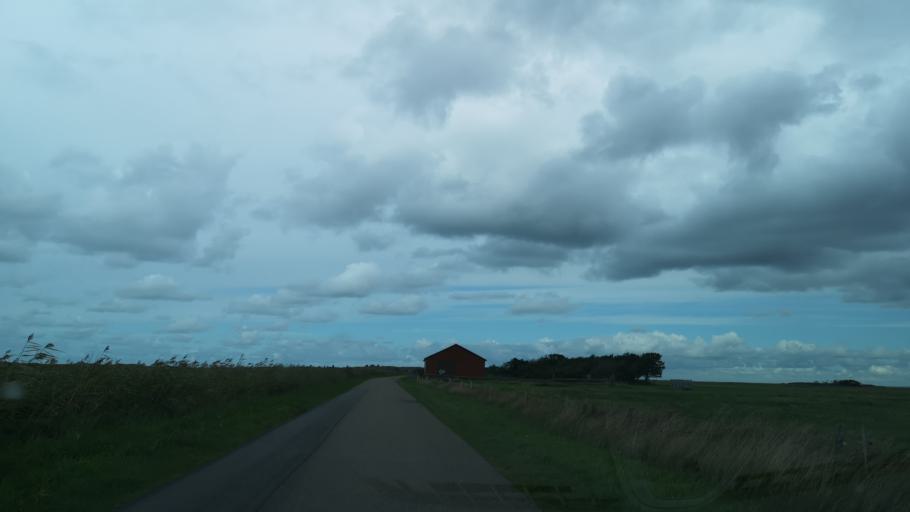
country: DK
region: Central Jutland
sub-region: Ringkobing-Skjern Kommune
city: Hvide Sande
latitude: 55.8401
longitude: 8.2174
